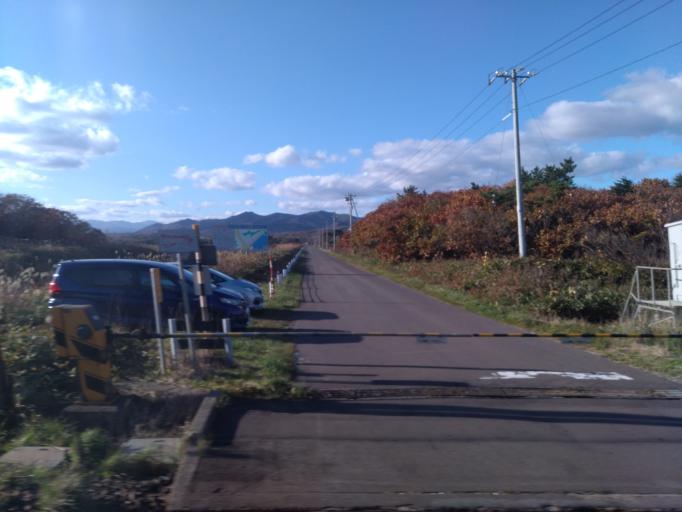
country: JP
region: Hokkaido
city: Niseko Town
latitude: 42.5534
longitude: 140.4212
